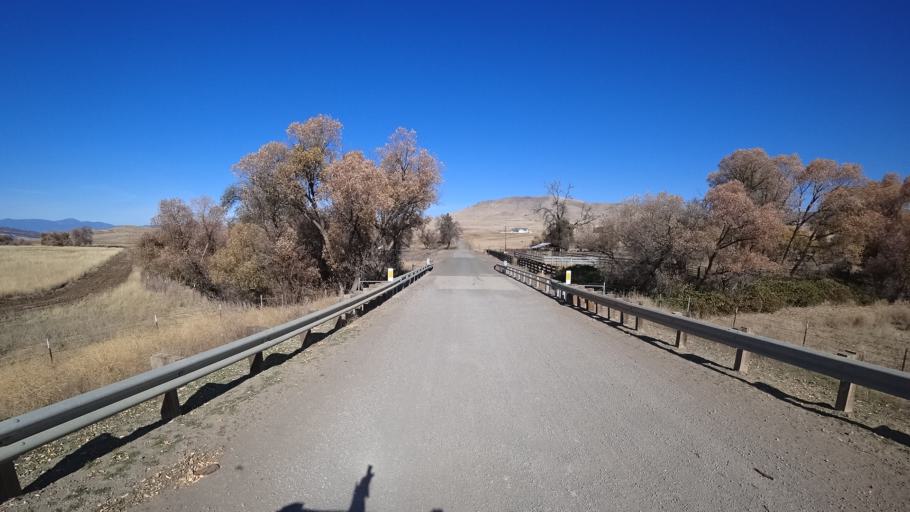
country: US
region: California
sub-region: Siskiyou County
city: Montague
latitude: 41.8212
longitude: -122.4213
